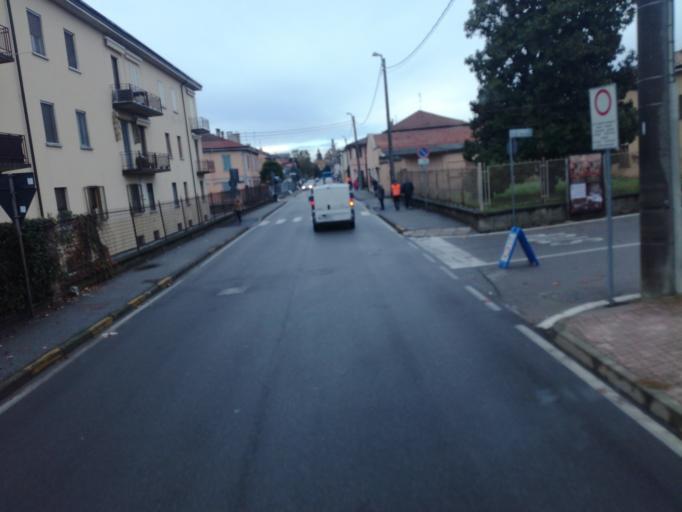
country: IT
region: Lombardy
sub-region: Provincia di Cremona
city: Spino d'Adda
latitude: 45.3965
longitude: 9.4903
